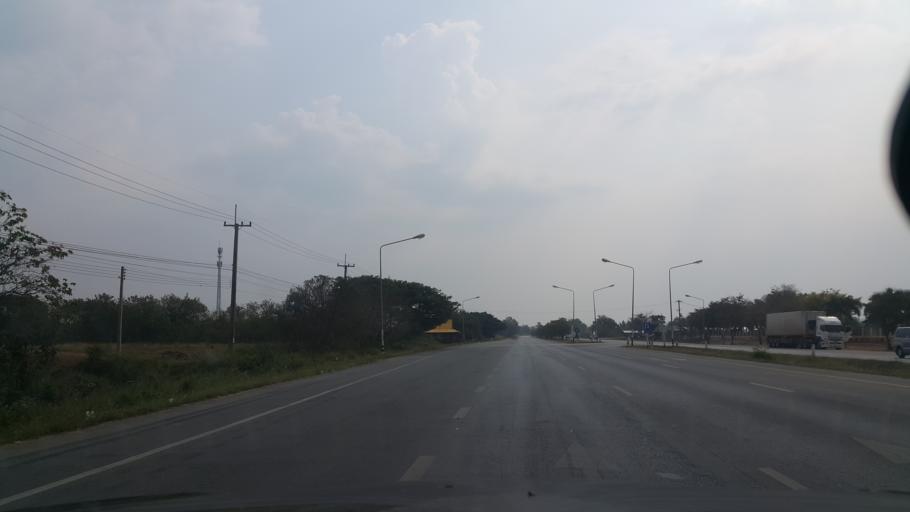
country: TH
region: Sukhothai
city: Sukhothai
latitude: 17.0610
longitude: 99.8896
